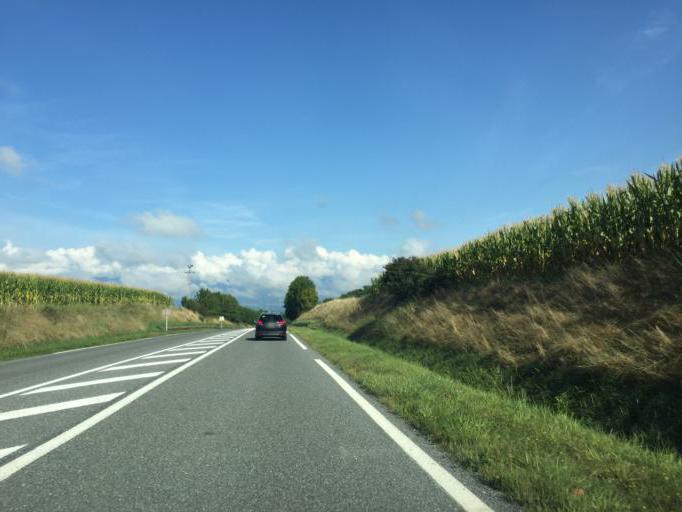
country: FR
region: Rhone-Alpes
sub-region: Departement de la Haute-Savoie
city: Beaumont
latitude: 46.1027
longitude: 6.1002
